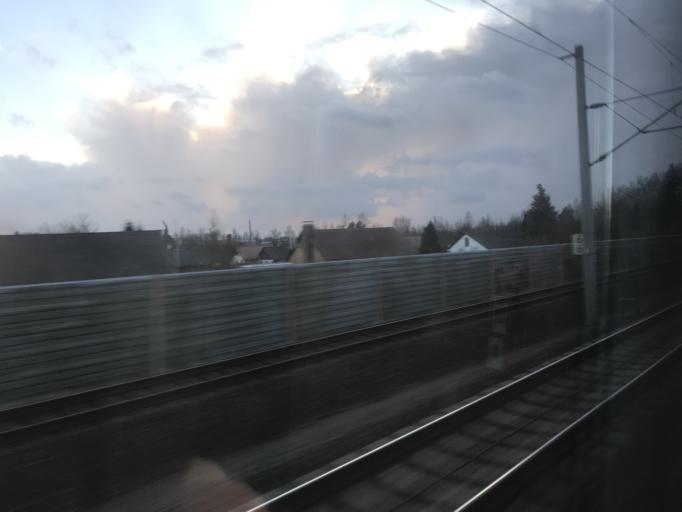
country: DE
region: Lower Saxony
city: Danndorf
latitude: 52.4313
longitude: 10.8762
